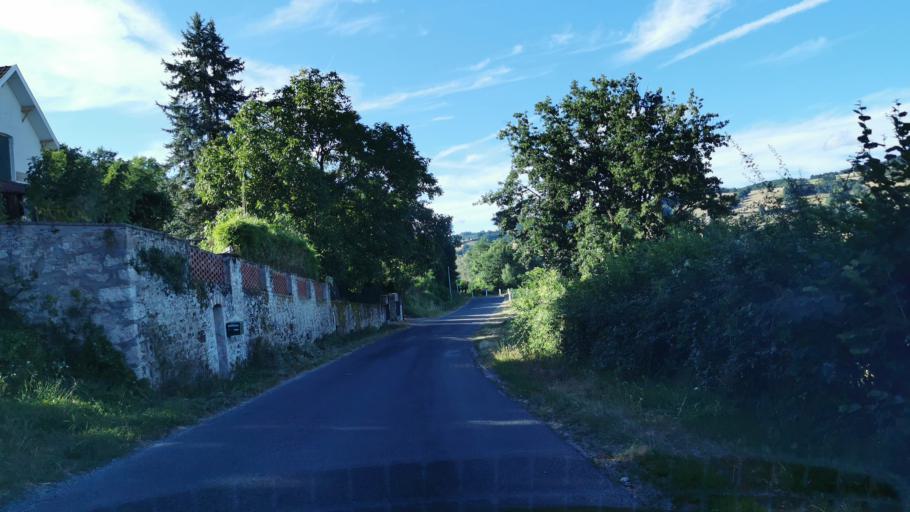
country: FR
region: Bourgogne
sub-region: Departement de Saone-et-Loire
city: Marmagne
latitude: 46.8416
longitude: 4.3275
